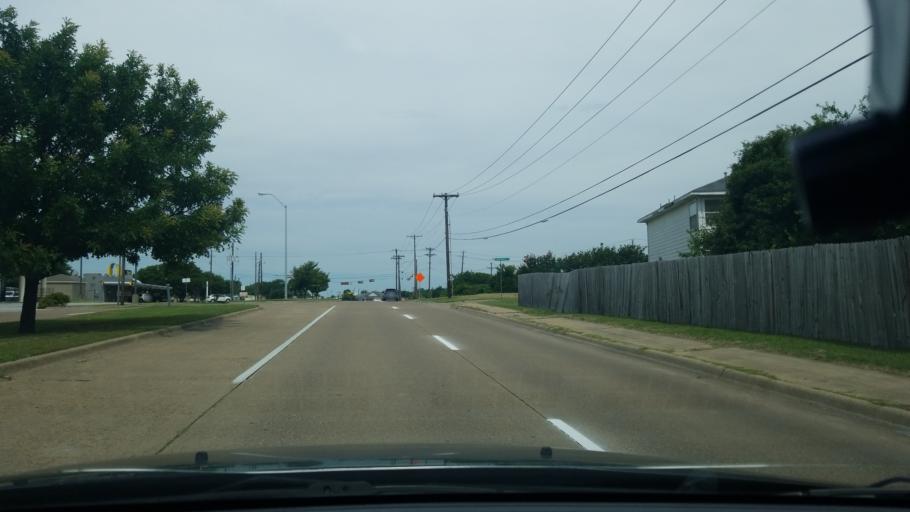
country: US
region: Texas
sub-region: Dallas County
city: Mesquite
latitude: 32.7637
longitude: -96.5803
